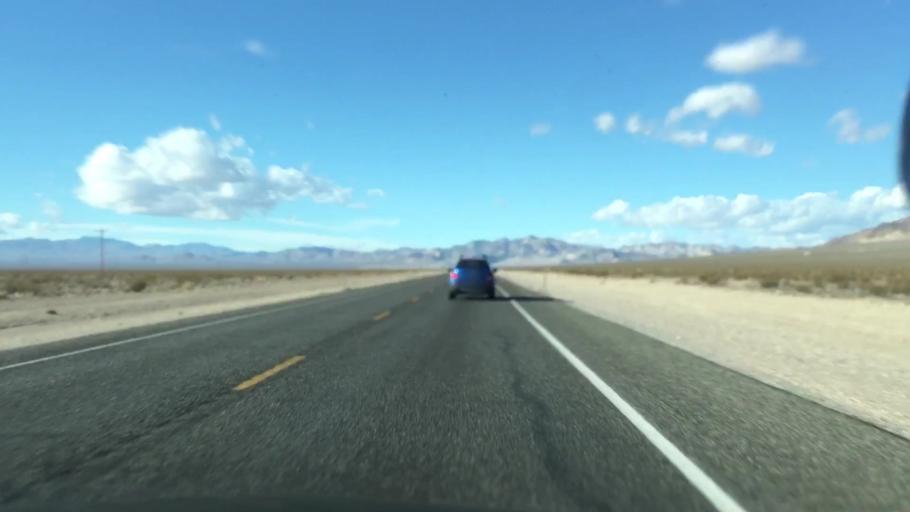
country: US
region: Nevada
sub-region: Nye County
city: Beatty
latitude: 36.7910
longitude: -116.7058
